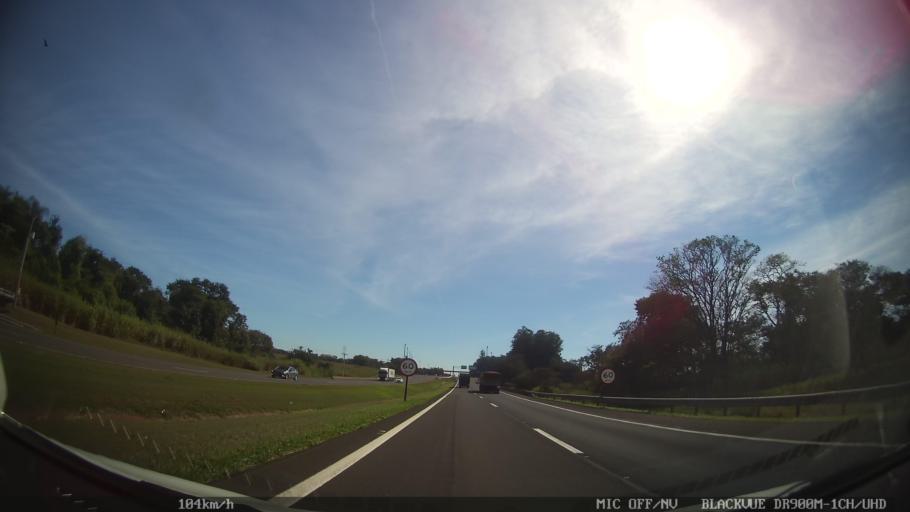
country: BR
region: Sao Paulo
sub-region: Pirassununga
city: Pirassununga
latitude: -21.9625
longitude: -47.4579
